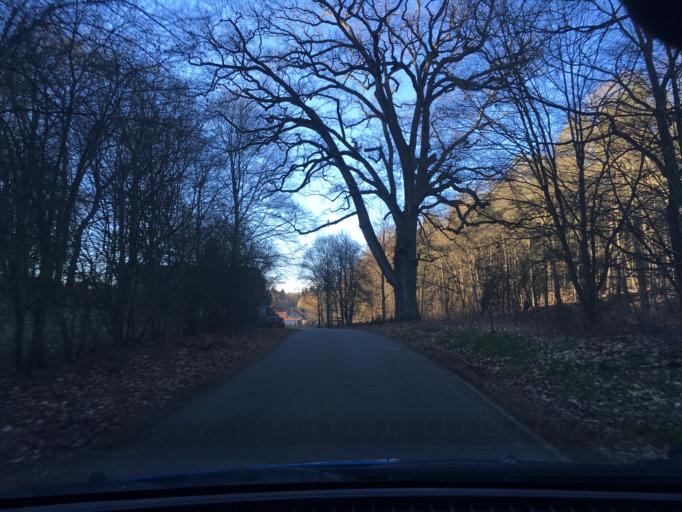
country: DE
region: Schleswig-Holstein
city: Schnakenbek
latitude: 53.3773
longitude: 10.5117
